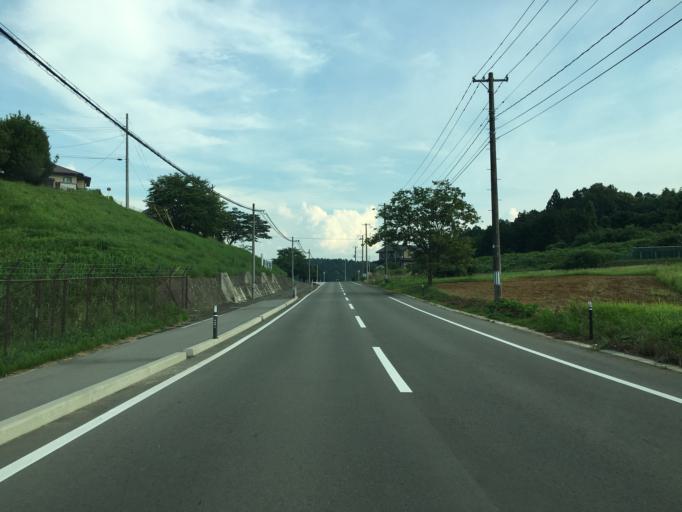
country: JP
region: Fukushima
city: Nihommatsu
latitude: 37.5582
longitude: 140.4302
